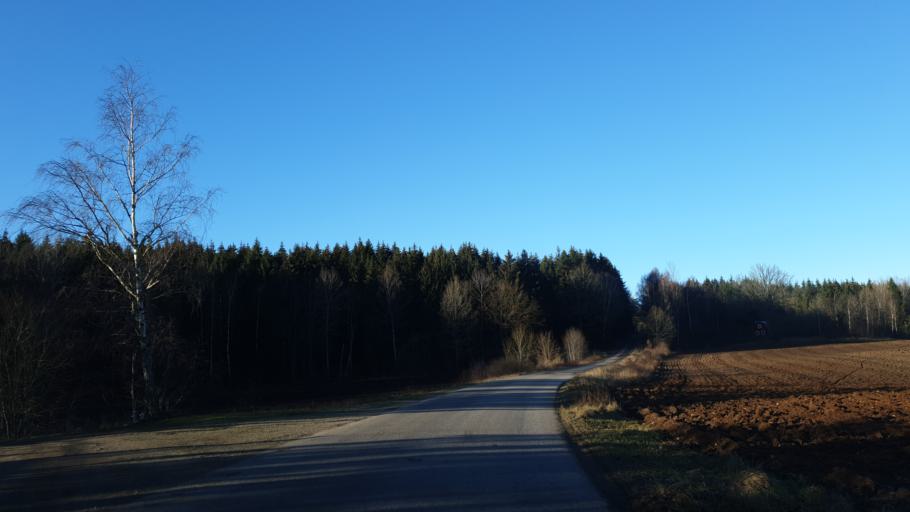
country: SE
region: Blekinge
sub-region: Karlskrona Kommun
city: Nattraby
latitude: 56.2614
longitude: 15.4883
